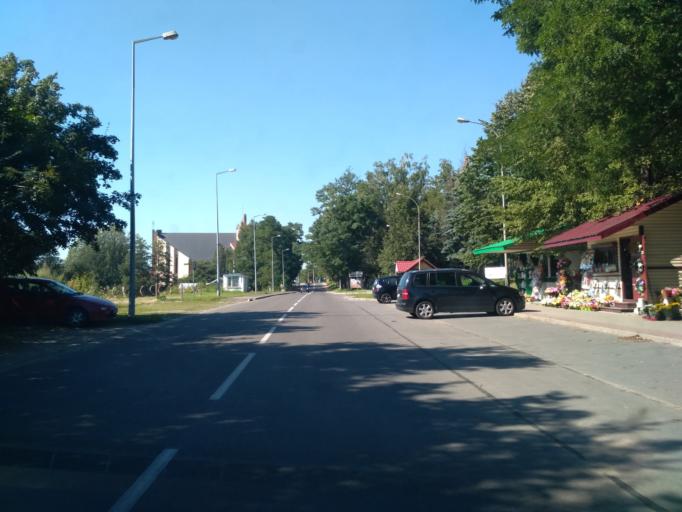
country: PL
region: Subcarpathian Voivodeship
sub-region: Krosno
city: Krosno
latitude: 49.6776
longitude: 21.7677
